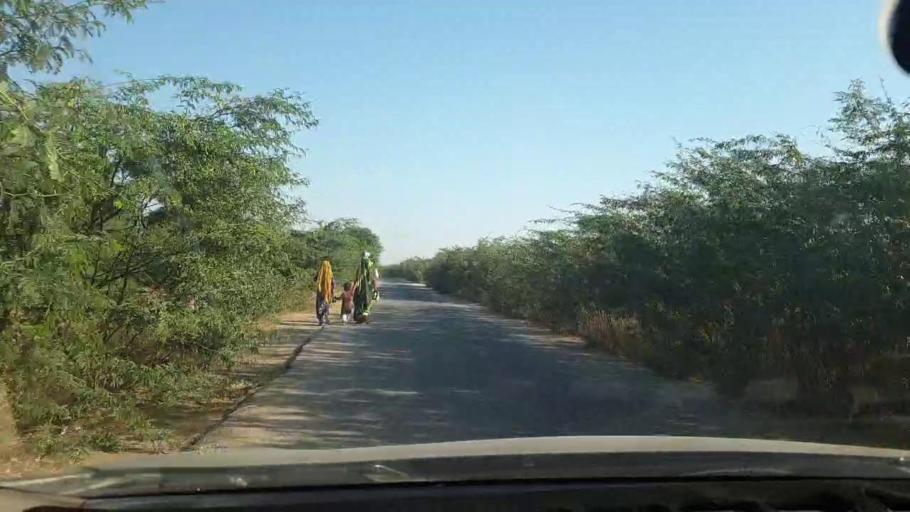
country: PK
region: Sindh
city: Malir Cantonment
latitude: 25.1490
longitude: 67.1888
